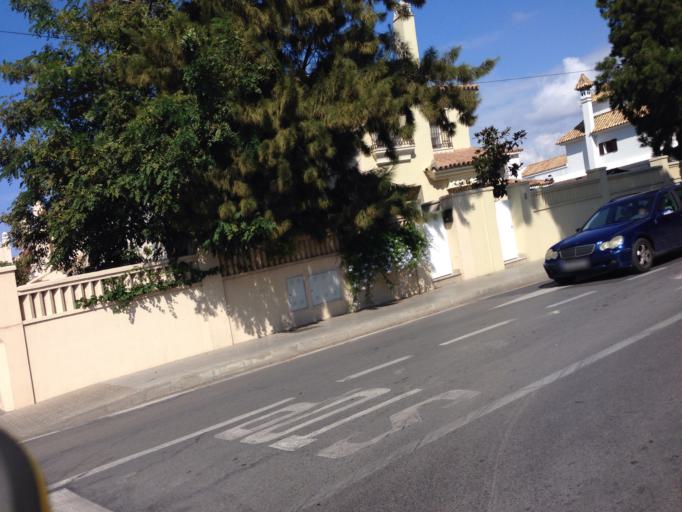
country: ES
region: Andalusia
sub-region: Provincia de Cadiz
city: Chiclana de la Frontera
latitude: 36.4166
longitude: -6.1558
